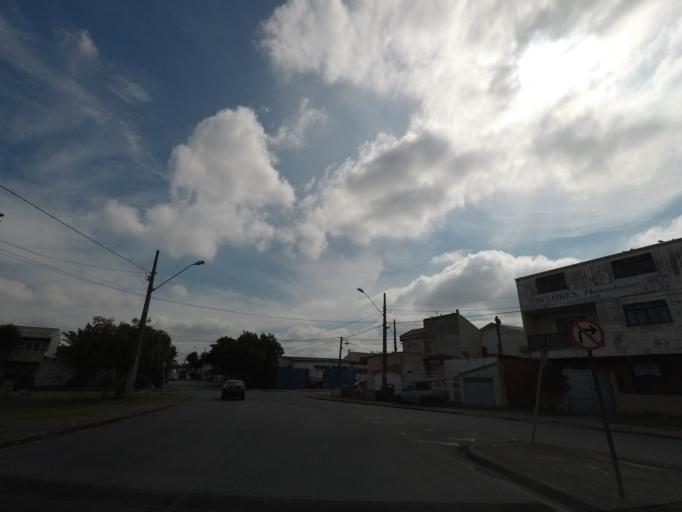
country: BR
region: Parana
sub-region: Curitiba
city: Curitiba
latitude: -25.4800
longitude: -49.2732
